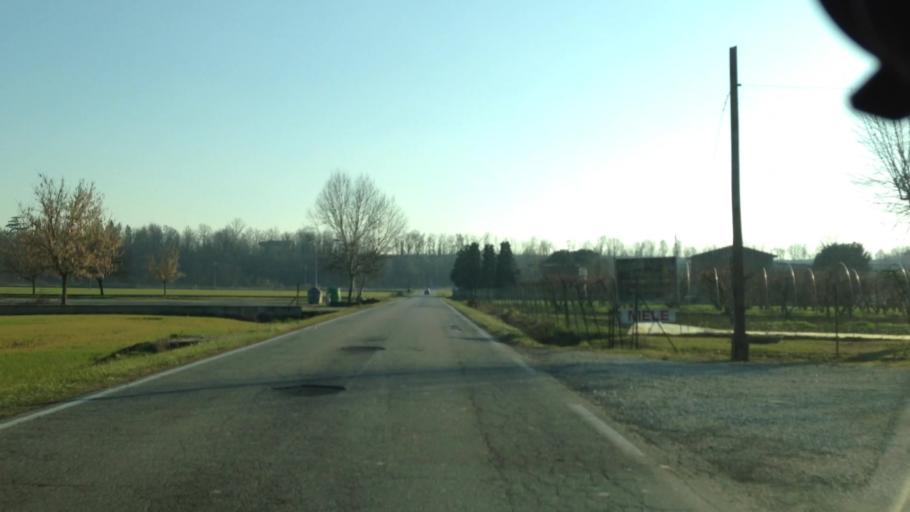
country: IT
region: Piedmont
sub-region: Provincia di Alessandria
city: Felizzano
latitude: 44.8772
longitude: 8.4446
